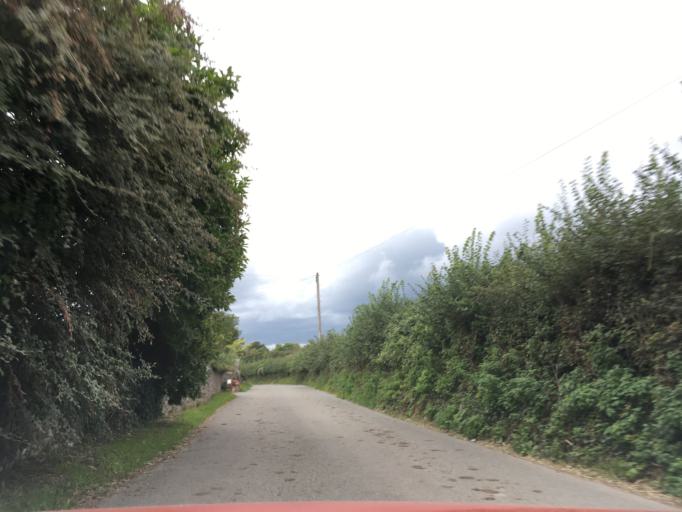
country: GB
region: Wales
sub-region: Monmouthshire
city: Chepstow
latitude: 51.6162
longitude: -2.6881
